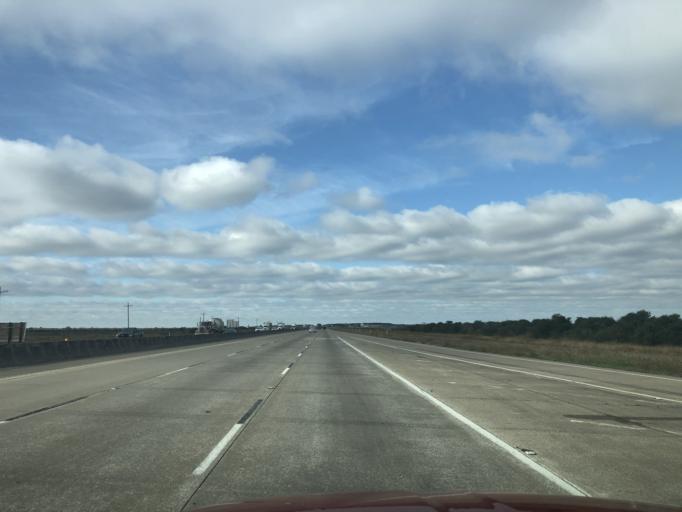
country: US
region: Texas
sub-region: Chambers County
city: Anahuac
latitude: 29.8350
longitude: -94.5447
